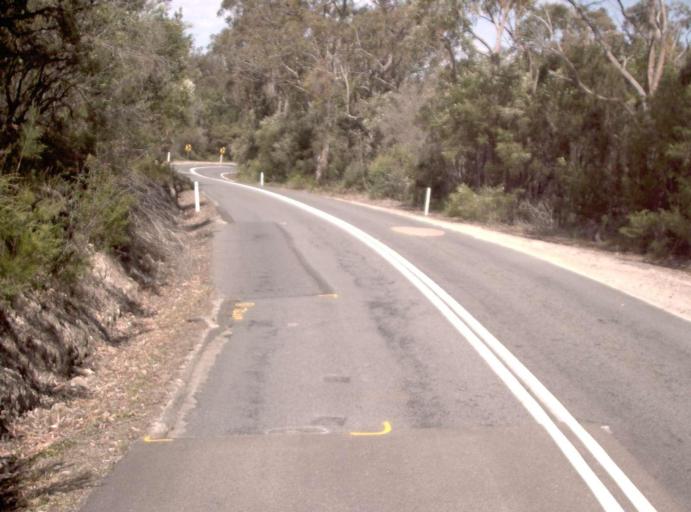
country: AU
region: New South Wales
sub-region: Bega Valley
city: Eden
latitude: -37.4956
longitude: 149.6639
